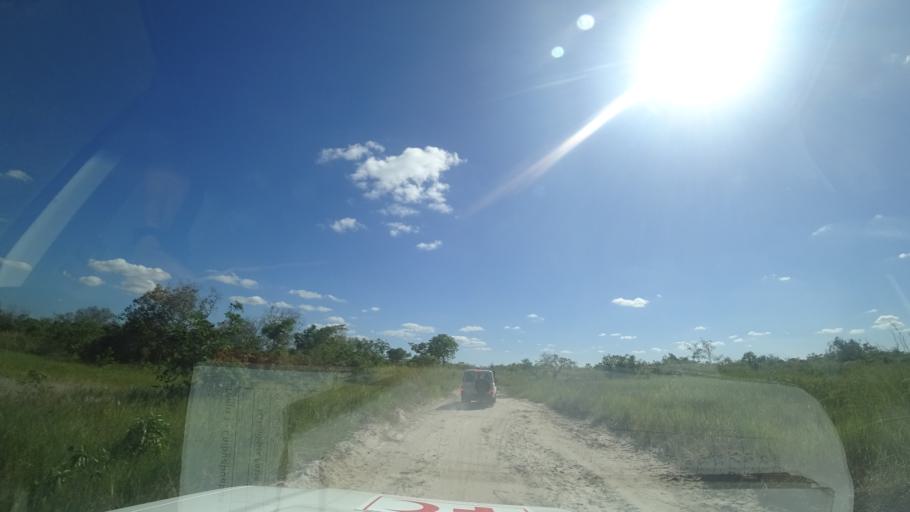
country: MZ
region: Sofala
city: Dondo
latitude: -19.4815
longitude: 34.6241
